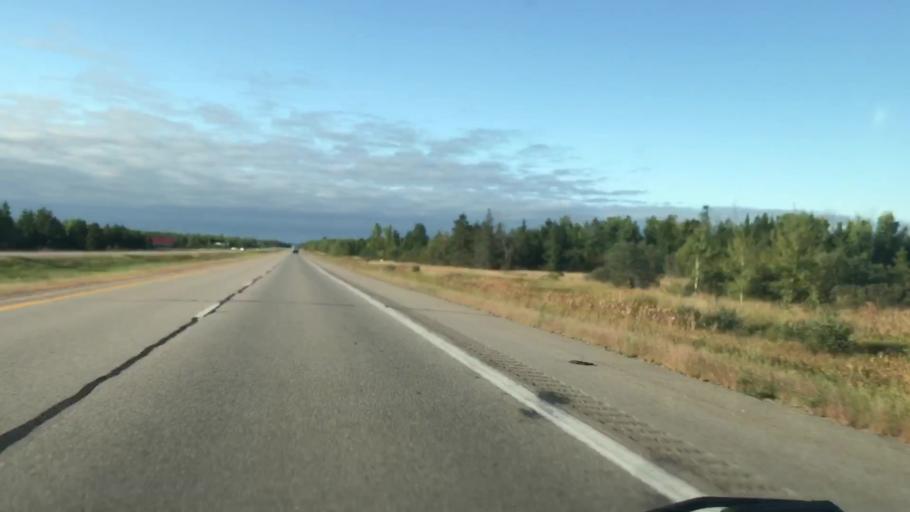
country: US
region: Michigan
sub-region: Chippewa County
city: Sault Ste. Marie
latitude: 46.4121
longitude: -84.3983
